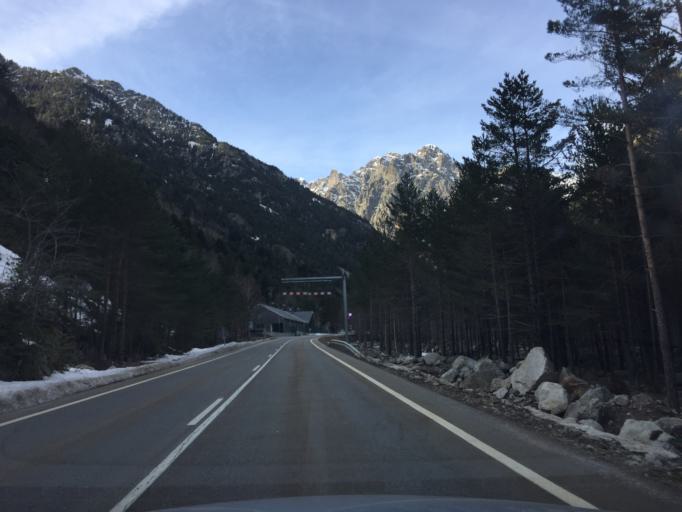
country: ES
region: Aragon
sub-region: Provincia de Huesca
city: Bielsa
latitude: 42.6877
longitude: 0.2095
